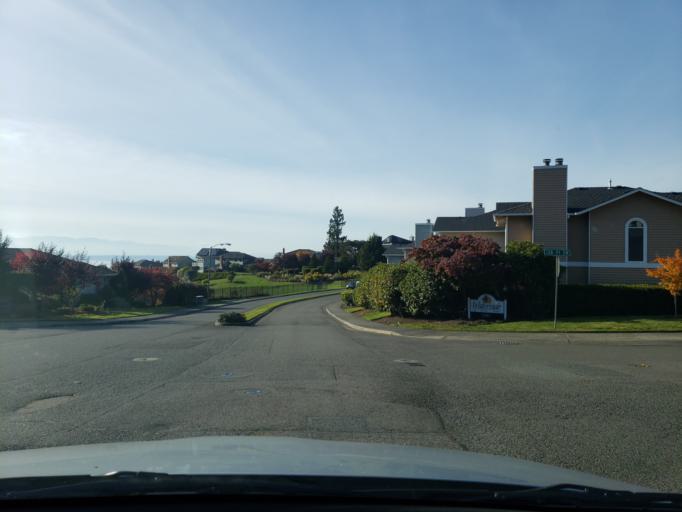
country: US
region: Washington
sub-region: Snohomish County
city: Meadowdale
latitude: 47.8728
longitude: -122.3195
